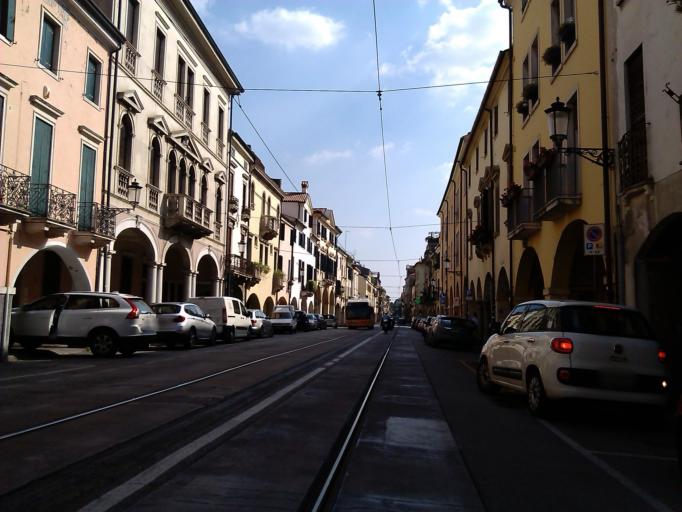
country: IT
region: Veneto
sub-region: Provincia di Padova
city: Padova
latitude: 45.3967
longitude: 11.8738
